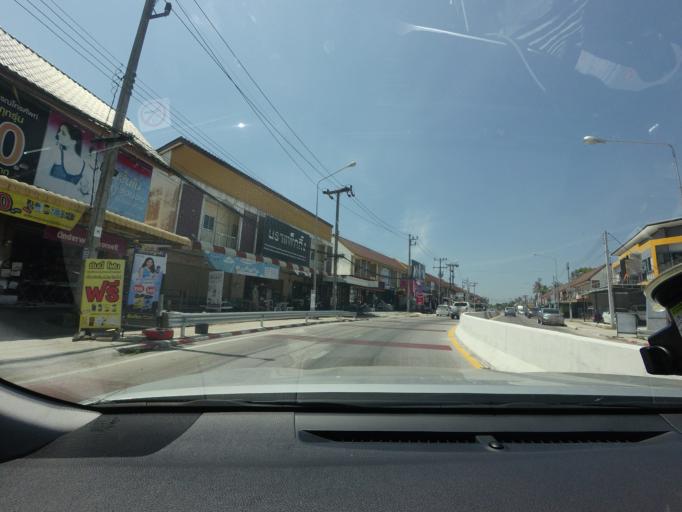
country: TH
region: Narathiwat
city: Narathiwat
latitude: 6.4250
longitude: 101.8191
